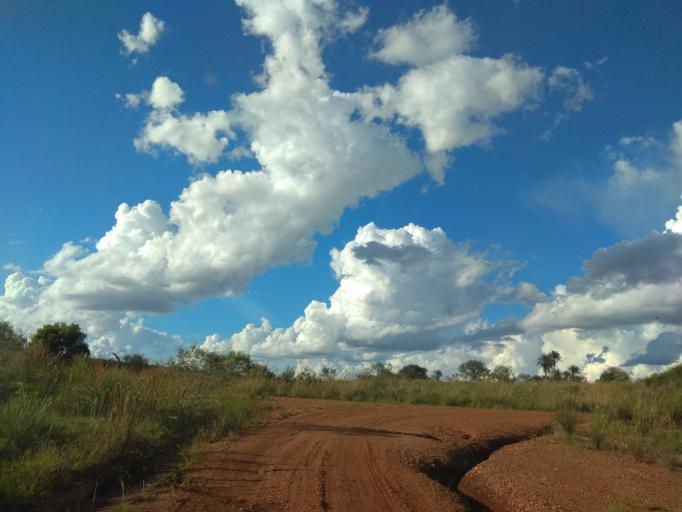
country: AR
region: Misiones
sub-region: Departamento de Candelaria
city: Candelaria
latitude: -27.4889
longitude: -55.7579
